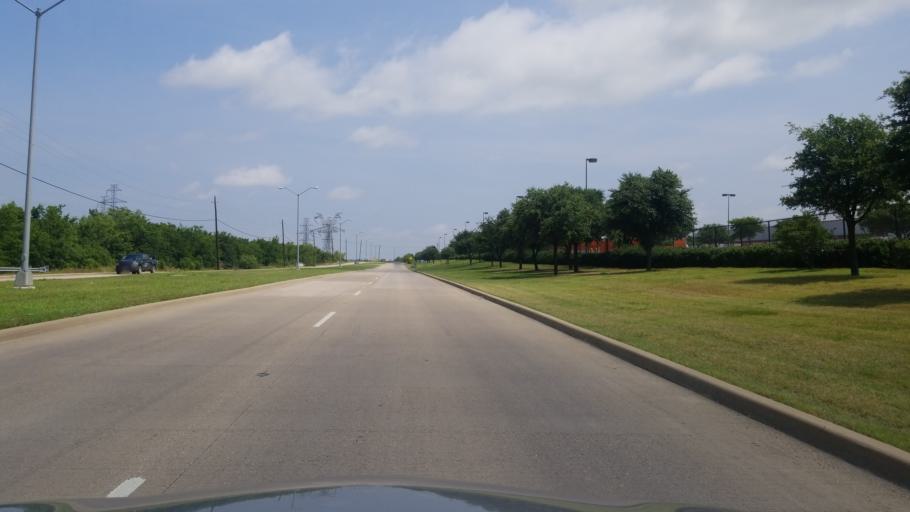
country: US
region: Texas
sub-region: Dallas County
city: Grand Prairie
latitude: 32.6927
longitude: -96.9630
